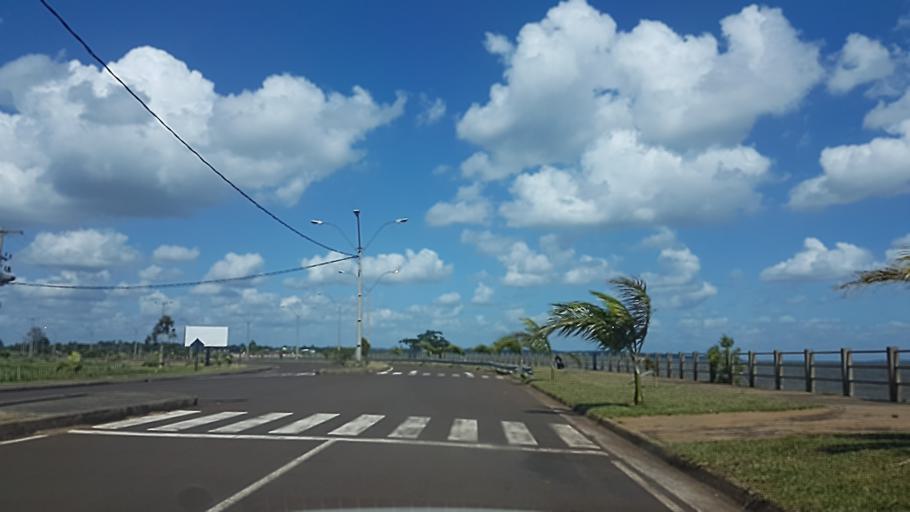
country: PY
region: Itapua
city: Carmen del Parana
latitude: -27.2269
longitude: -56.1720
